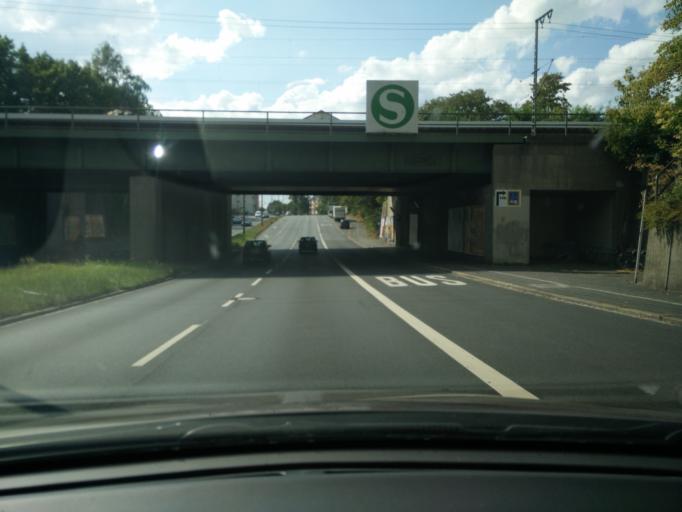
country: DE
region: Bavaria
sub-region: Regierungsbezirk Mittelfranken
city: Nuernberg
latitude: 49.4295
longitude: 11.0555
